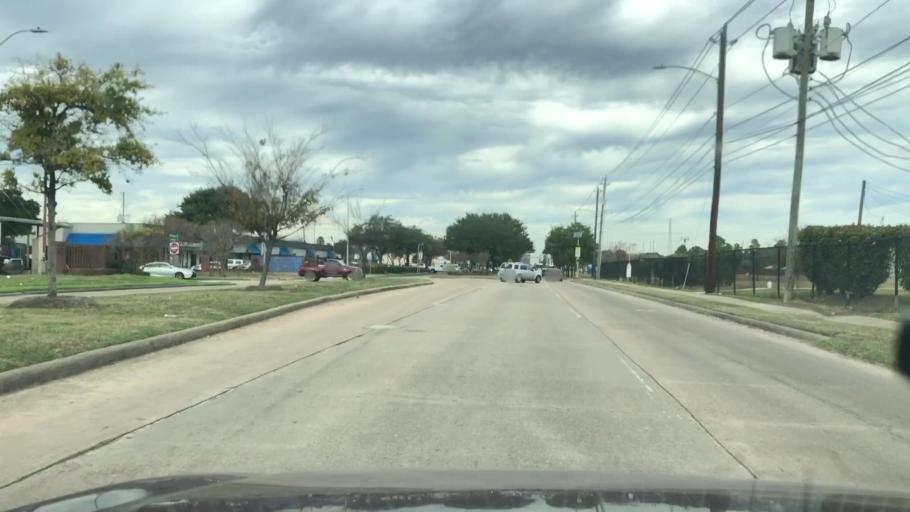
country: US
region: Texas
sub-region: Fort Bend County
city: Missouri City
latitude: 29.6622
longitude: -95.5280
